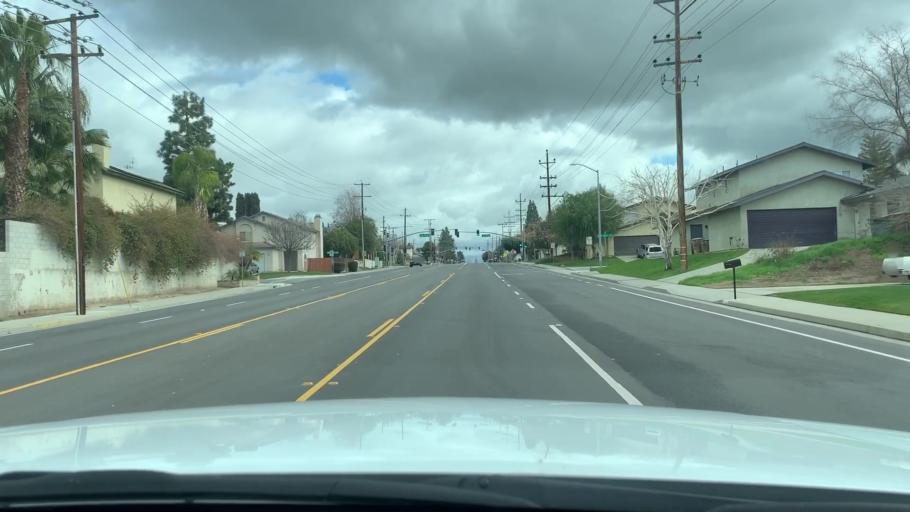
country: US
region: California
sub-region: Kern County
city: Bakersfield
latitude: 35.3978
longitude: -118.9427
